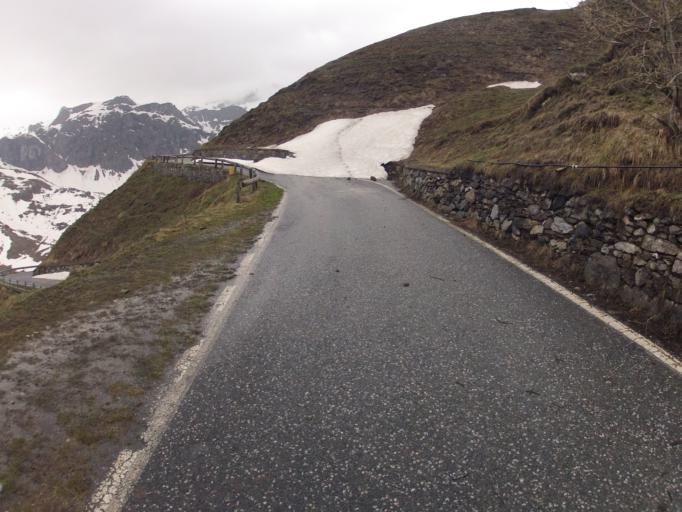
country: IT
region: Piedmont
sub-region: Provincia di Cuneo
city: Crissolo
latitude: 44.7036
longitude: 7.1176
